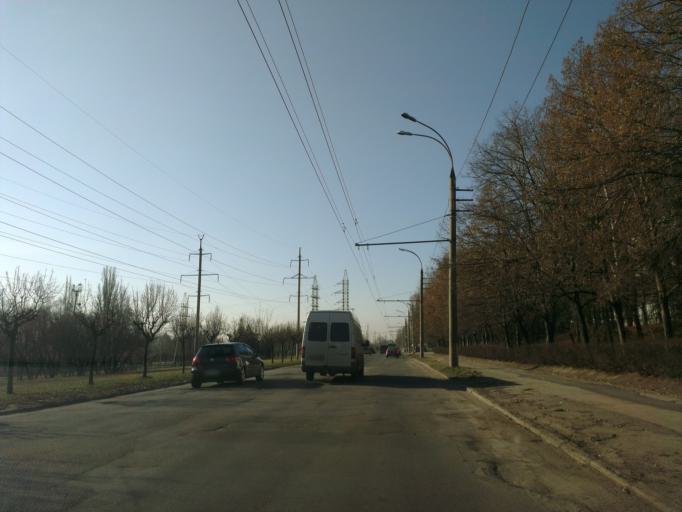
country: MD
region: Chisinau
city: Chisinau
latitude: 47.0216
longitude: 28.8876
